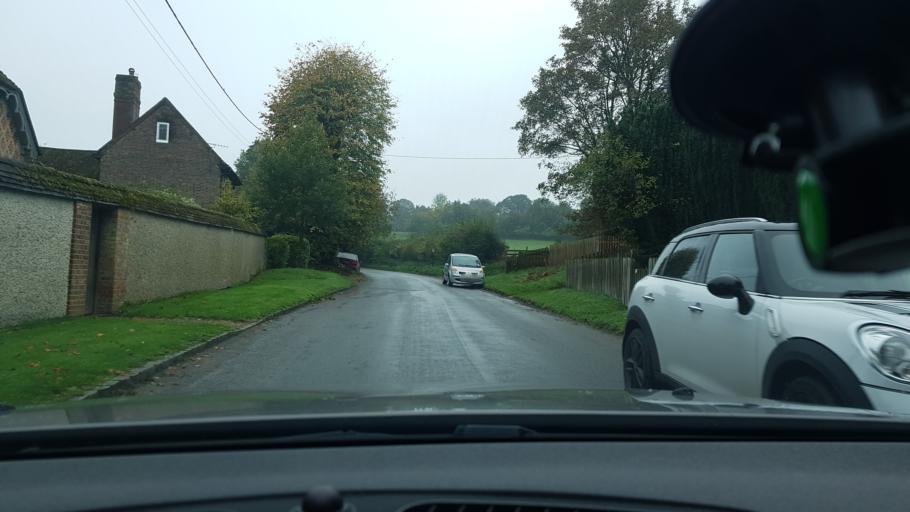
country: GB
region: England
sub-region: Wiltshire
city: Burbage
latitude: 51.3757
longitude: -1.6601
